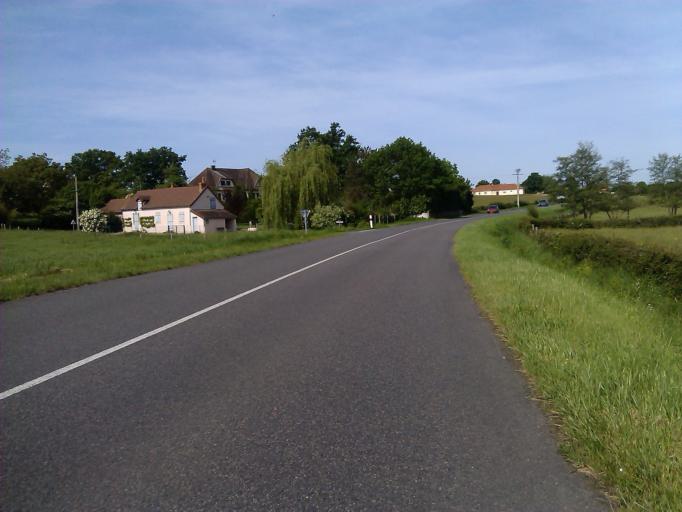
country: FR
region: Auvergne
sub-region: Departement de l'Allier
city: Dompierre-sur-Besbre
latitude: 46.5312
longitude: 3.6618
